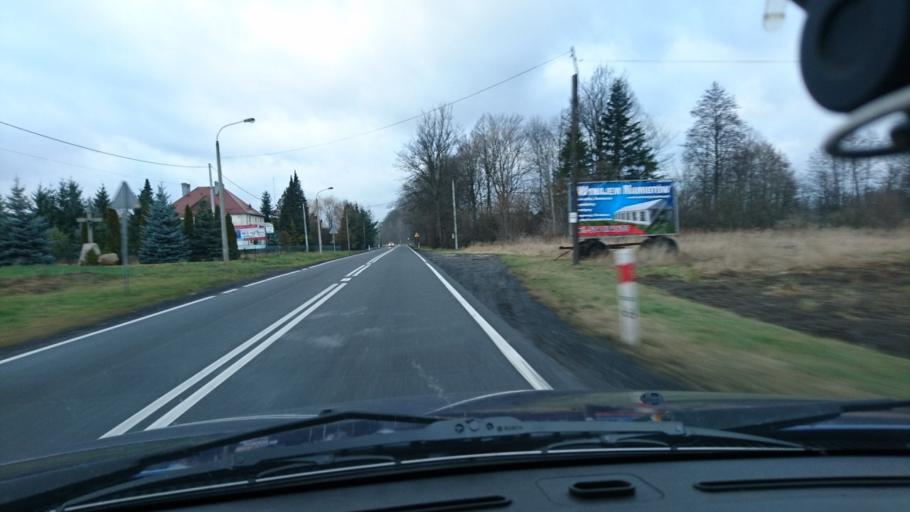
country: PL
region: Opole Voivodeship
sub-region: Powiat oleski
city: Olesno
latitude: 50.9142
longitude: 18.3484
